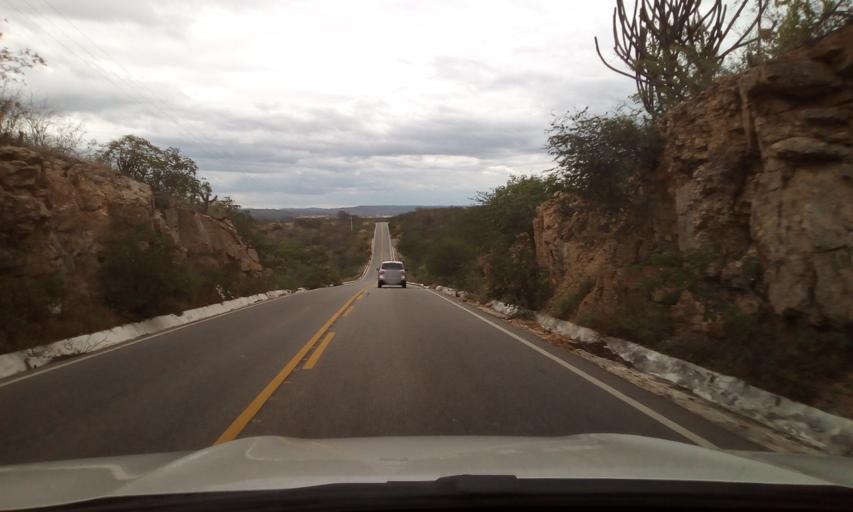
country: BR
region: Paraiba
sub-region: Picui
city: Picui
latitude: -6.5291
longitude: -36.3129
